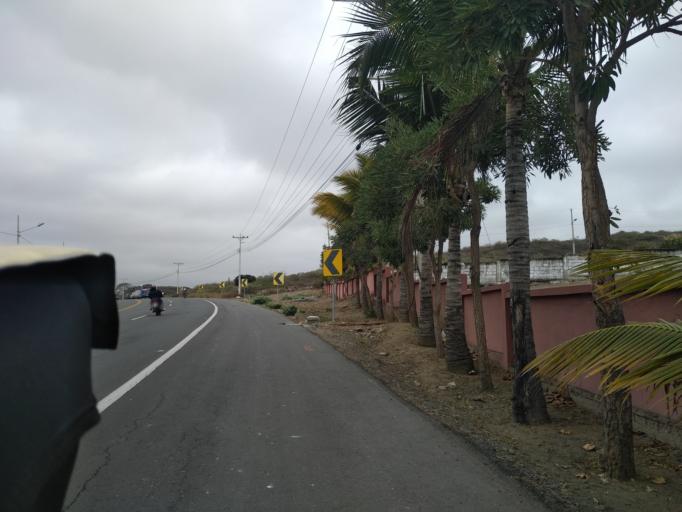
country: EC
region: Santa Elena
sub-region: Canton Santa Elena
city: Santa Elena
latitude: -2.1988
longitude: -80.8546
